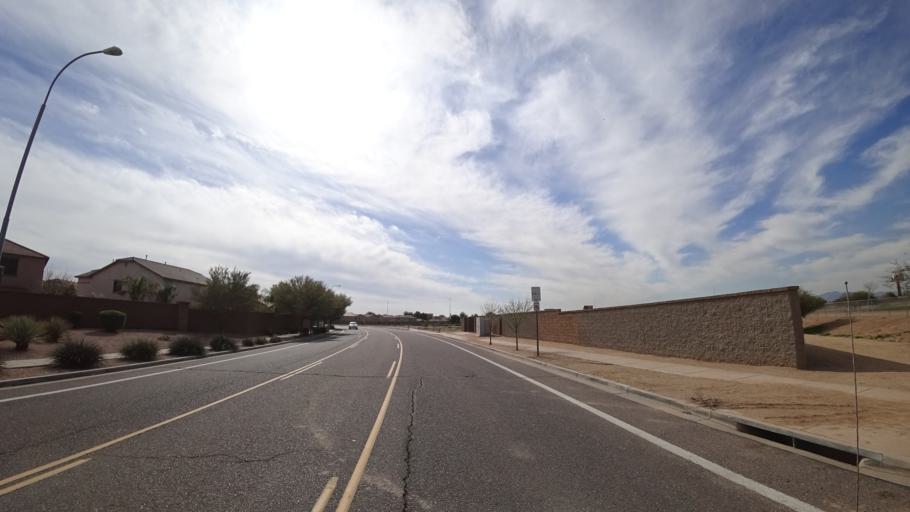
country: US
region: Arizona
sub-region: Maricopa County
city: Tolleson
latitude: 33.4724
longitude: -112.2632
